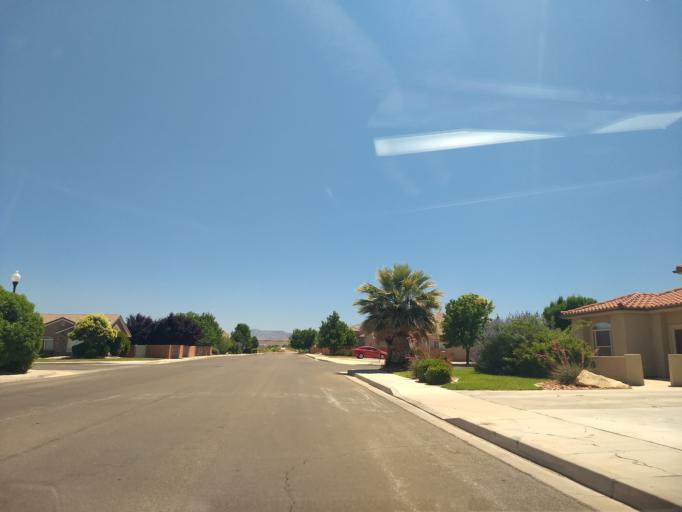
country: US
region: Utah
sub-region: Washington County
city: Washington
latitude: 37.0984
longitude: -113.5136
